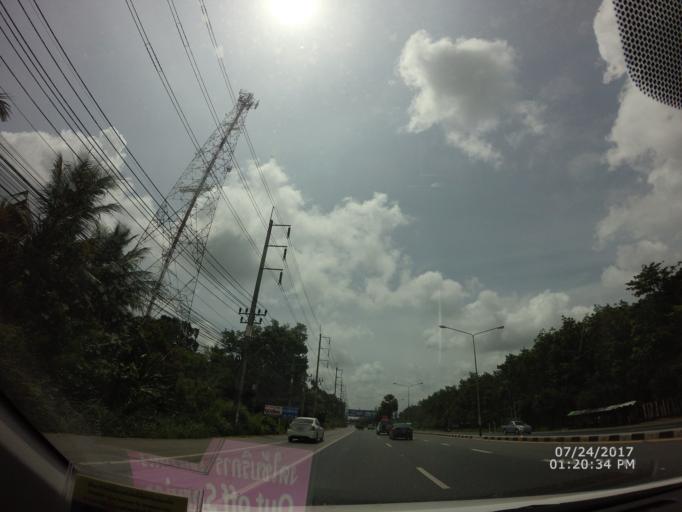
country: TH
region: Phuket
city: Thalang
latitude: 8.0719
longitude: 98.3433
